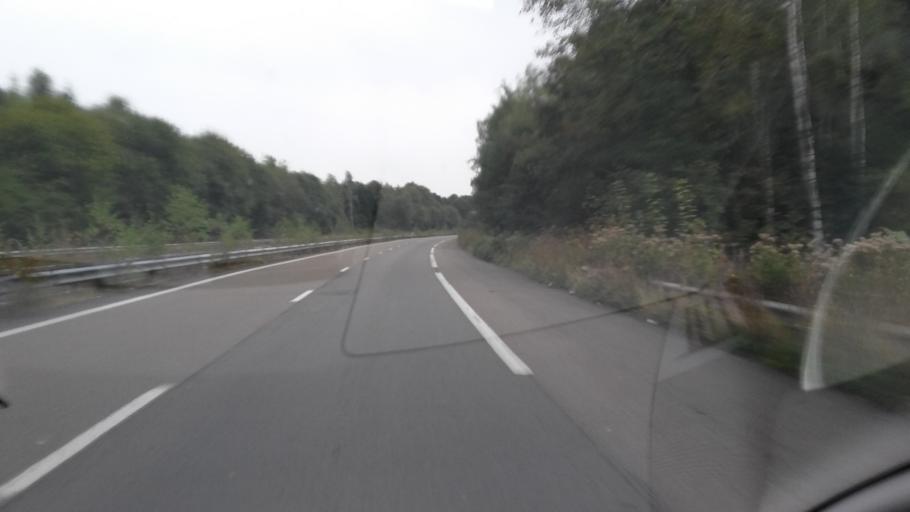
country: BE
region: Wallonia
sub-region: Province du Luxembourg
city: Bouillon
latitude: 49.7500
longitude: 5.0239
